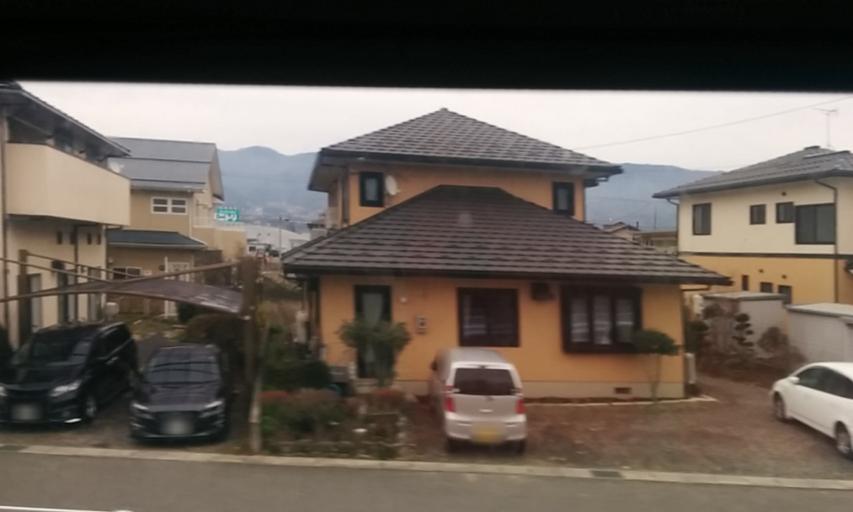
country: JP
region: Nagano
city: Matsumoto
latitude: 36.1853
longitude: 137.9605
